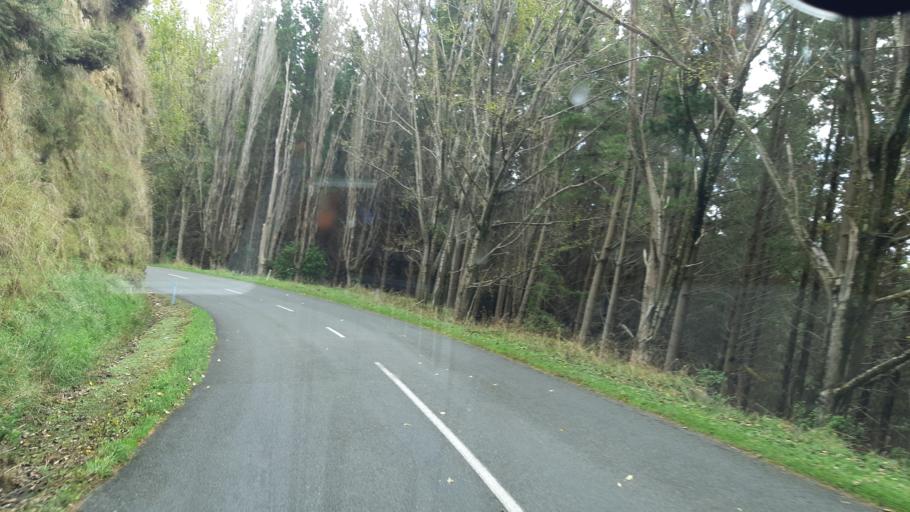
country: NZ
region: Manawatu-Wanganui
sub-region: Rangitikei District
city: Bulls
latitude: -39.9090
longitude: 175.5458
